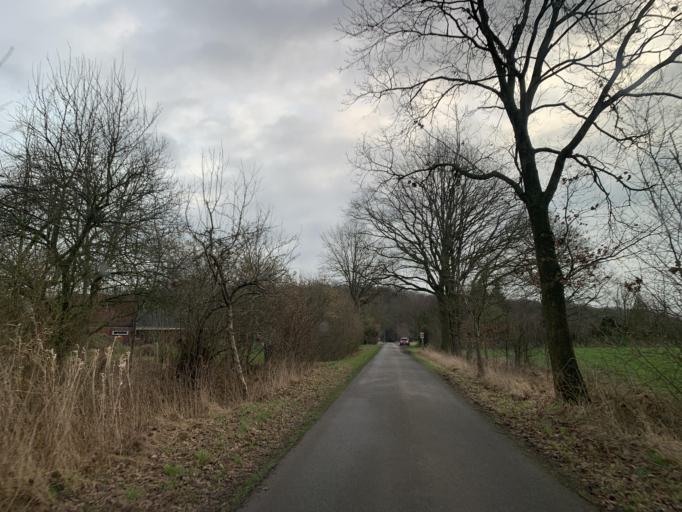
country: DE
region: North Rhine-Westphalia
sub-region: Regierungsbezirk Munster
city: Senden
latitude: 51.9213
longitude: 7.4878
